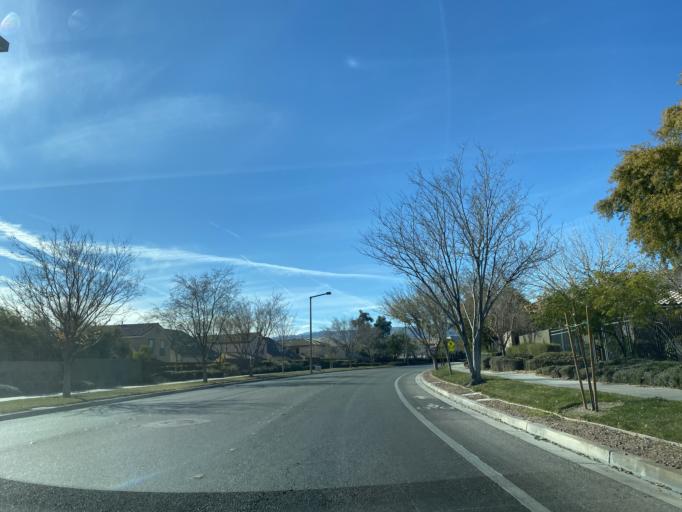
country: US
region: Nevada
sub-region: Clark County
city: Summerlin South
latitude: 36.1475
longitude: -115.3190
